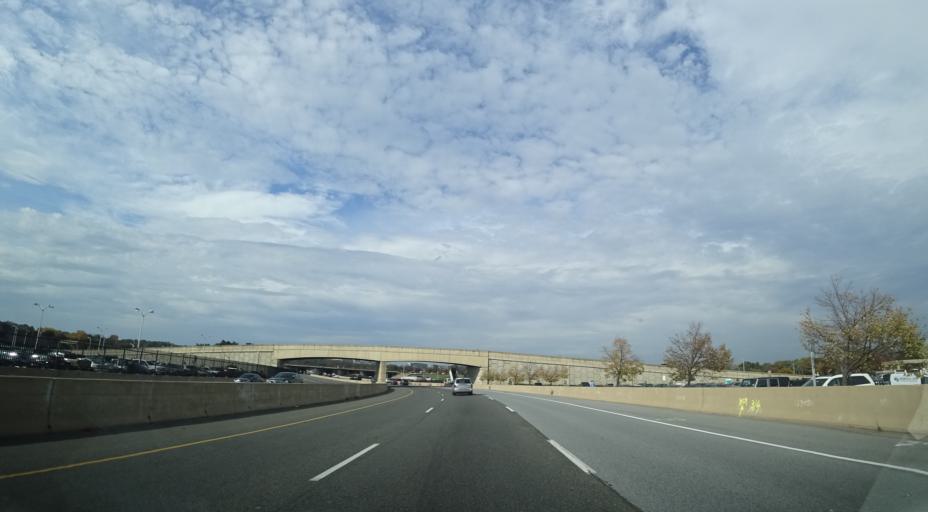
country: US
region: Washington, D.C.
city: Washington, D.C.
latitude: 38.8746
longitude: -77.0528
